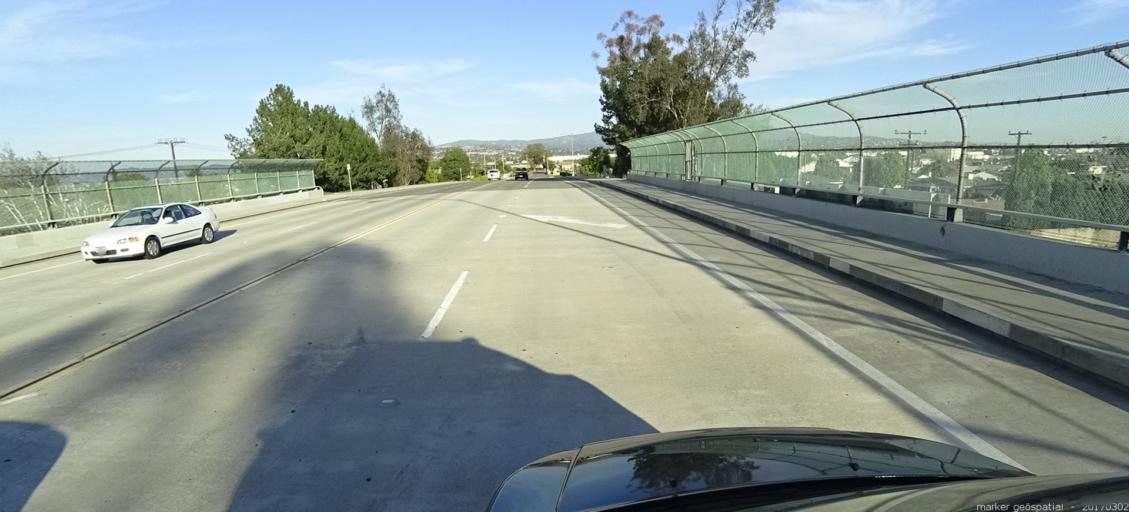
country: US
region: California
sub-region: Orange County
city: Anaheim
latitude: 33.8253
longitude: -117.8763
